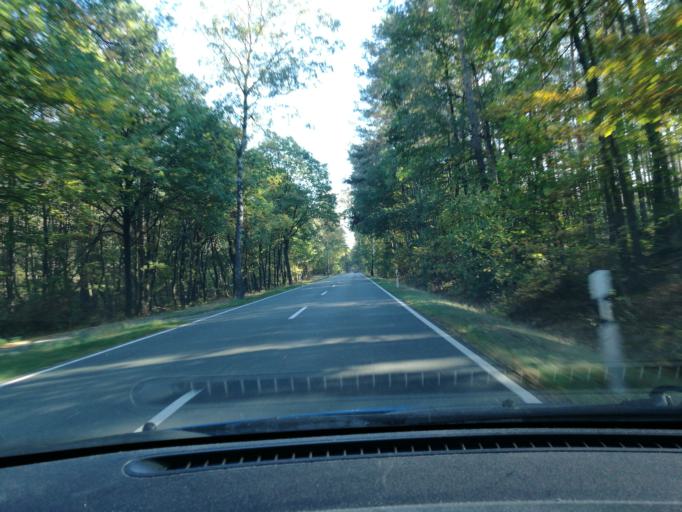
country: DE
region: Lower Saxony
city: Karwitz
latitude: 53.1232
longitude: 10.9825
